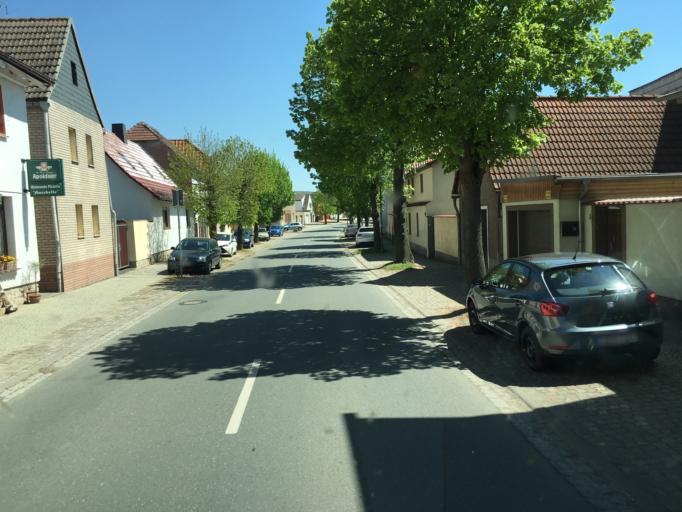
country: DE
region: Thuringia
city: Rossleben
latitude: 51.2957
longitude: 11.4360
